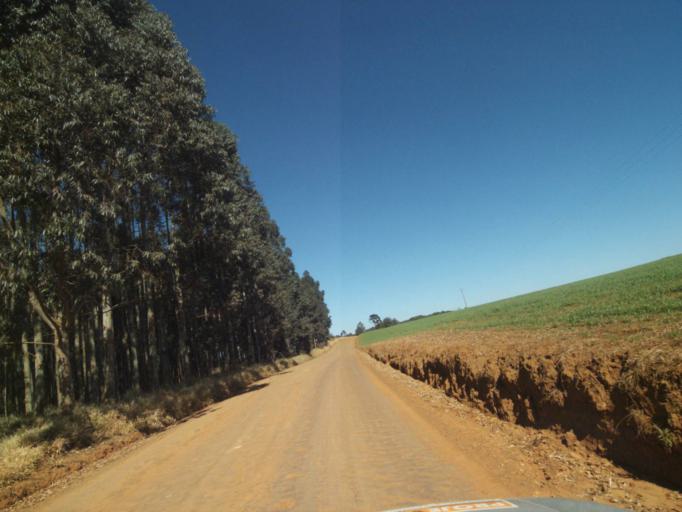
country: BR
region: Parana
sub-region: Tibagi
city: Tibagi
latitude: -24.6118
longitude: -50.6056
